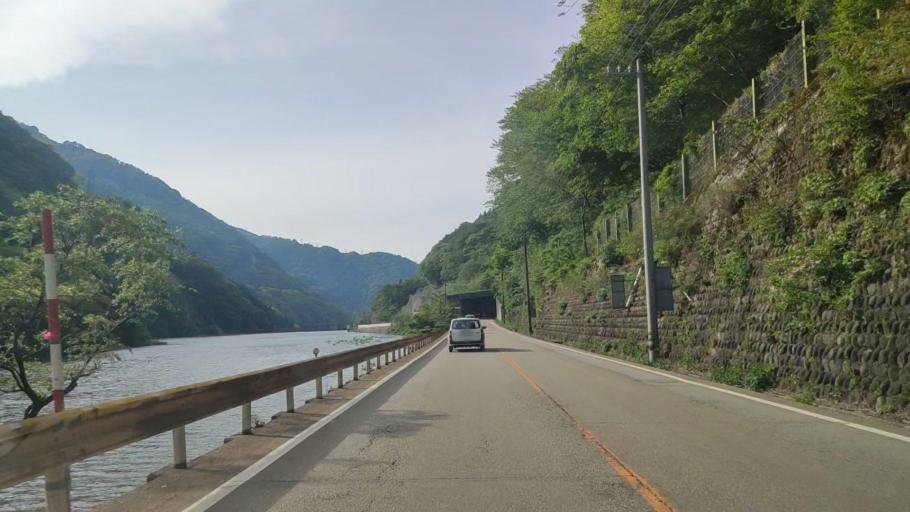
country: JP
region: Toyama
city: Yatsuomachi-higashikumisaka
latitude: 36.4233
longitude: 137.2849
